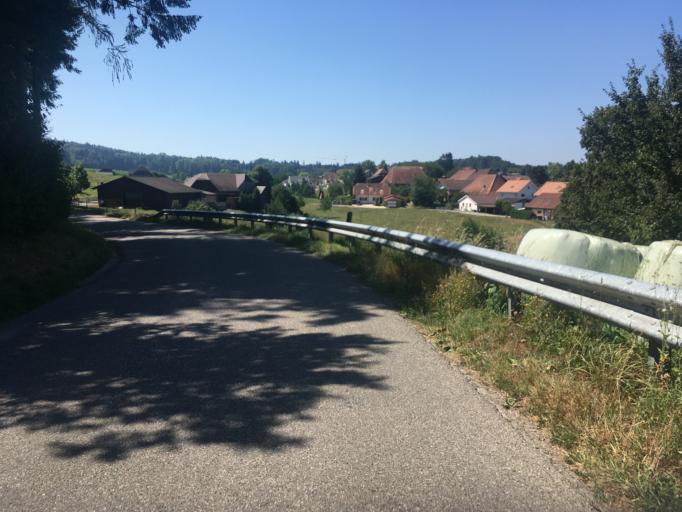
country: CH
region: Solothurn
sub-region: Bezirk Bucheggberg
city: Messen
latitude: 47.0870
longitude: 7.4823
